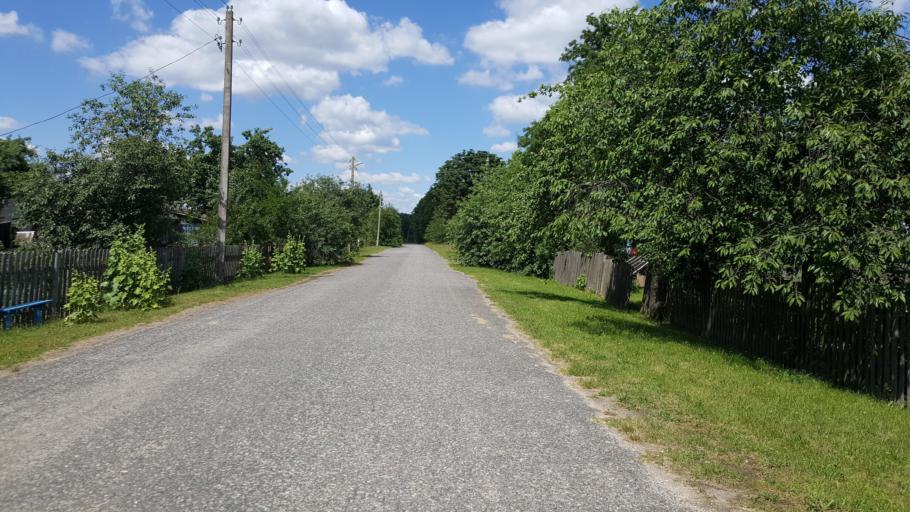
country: PL
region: Podlasie
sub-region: Powiat hajnowski
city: Czeremcha
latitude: 52.5096
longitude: 23.5479
